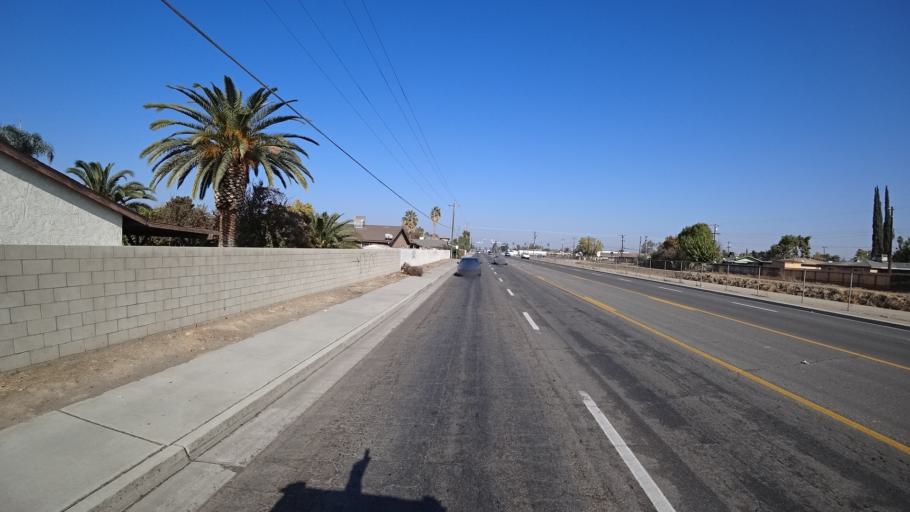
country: US
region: California
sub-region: Kern County
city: Greenfield
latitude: 35.3015
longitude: -119.0214
